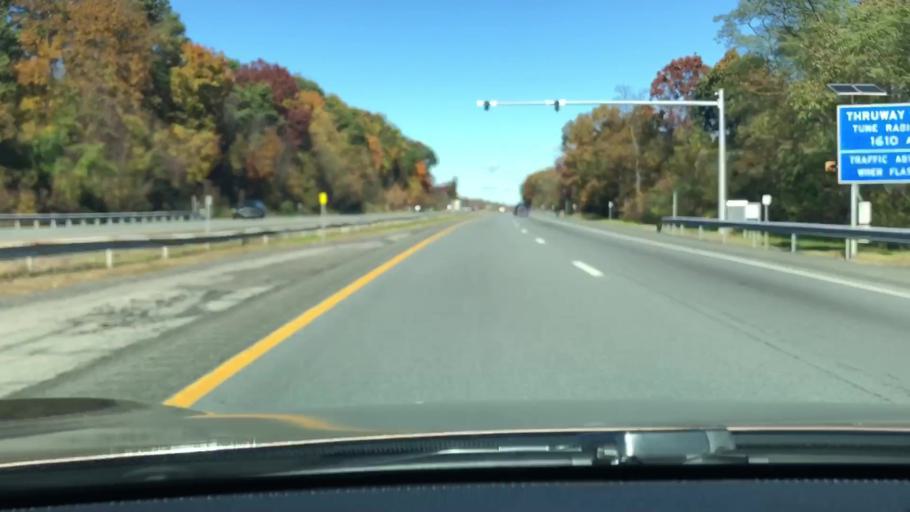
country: US
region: New York
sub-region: Orange County
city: Vails Gate
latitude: 41.4871
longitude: -74.0793
